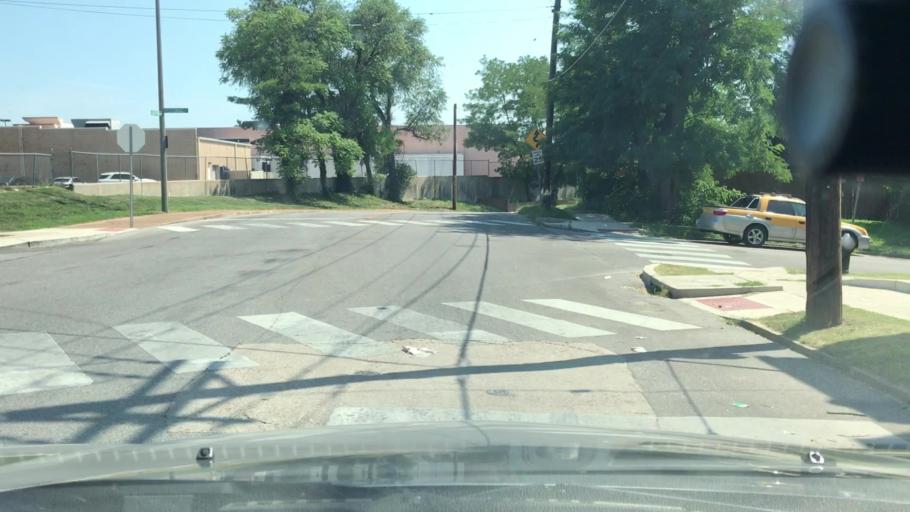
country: US
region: Missouri
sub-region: City of Saint Louis
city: St. Louis
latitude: 38.5946
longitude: -90.2510
